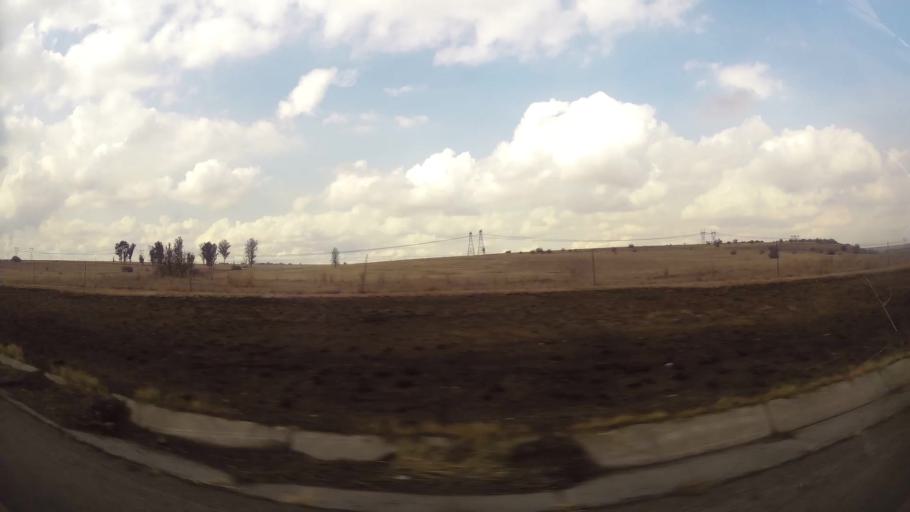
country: ZA
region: Orange Free State
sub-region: Fezile Dabi District Municipality
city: Sasolburg
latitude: -26.8010
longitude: 27.9136
